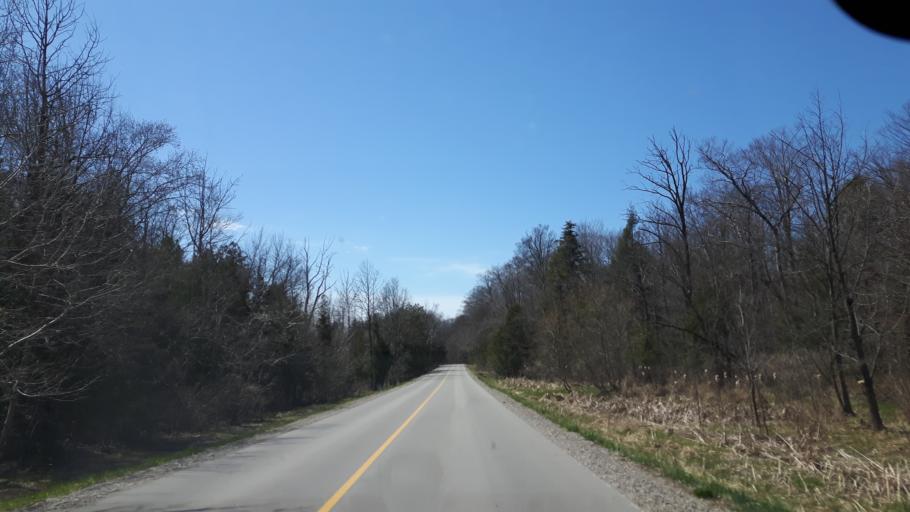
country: CA
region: Ontario
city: Bluewater
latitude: 43.5843
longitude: -81.6714
